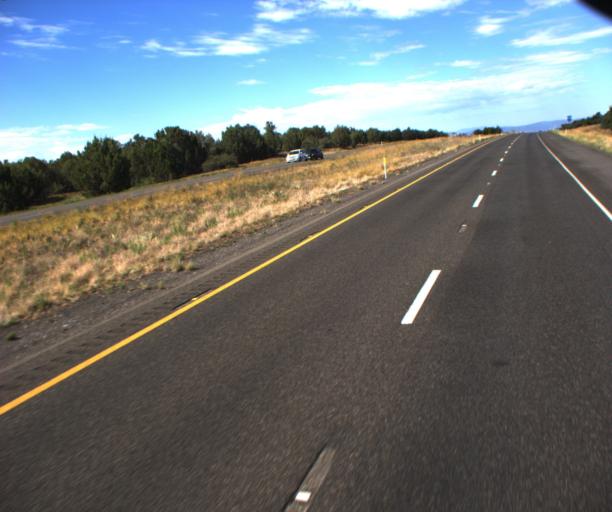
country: US
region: Arizona
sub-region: Yavapai County
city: Village of Oak Creek (Big Park)
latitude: 34.7598
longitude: -111.6627
